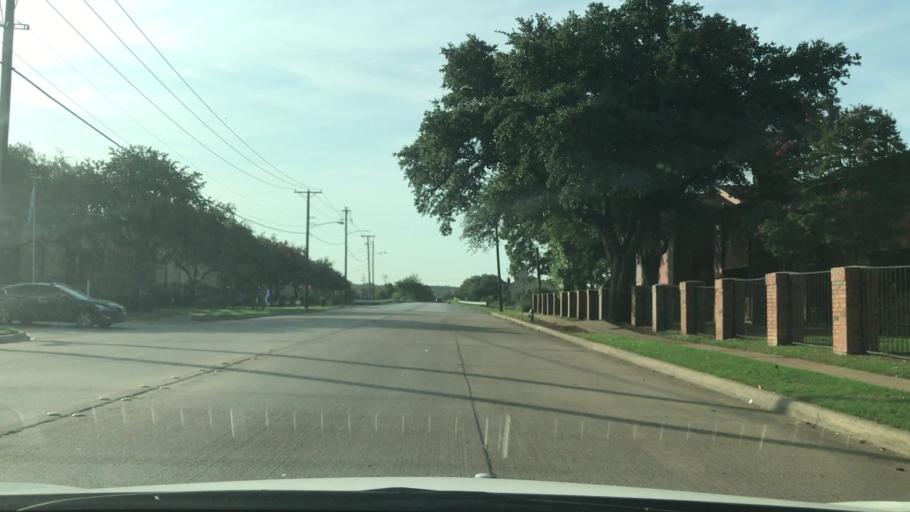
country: US
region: Texas
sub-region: Tarrant County
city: Pantego
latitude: 32.7617
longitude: -97.1601
